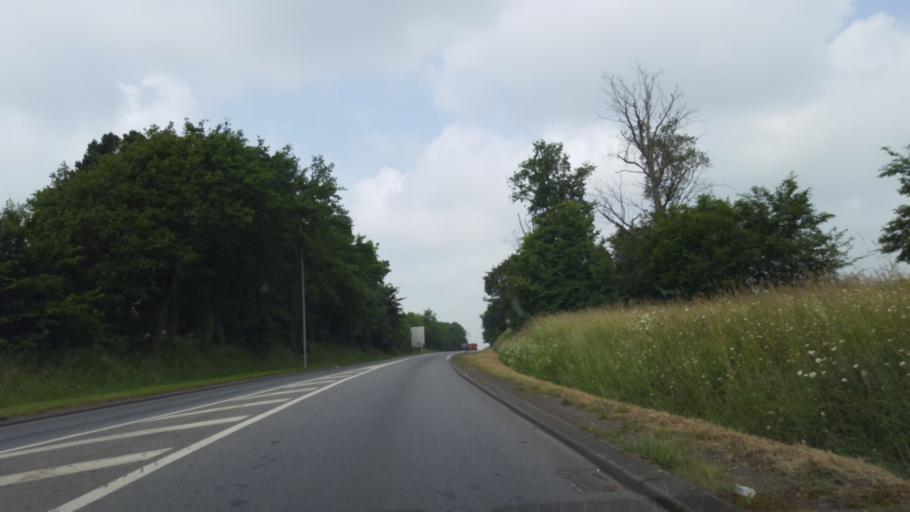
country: FR
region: Brittany
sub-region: Departement d'Ille-et-Vilaine
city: Chartres-de-Bretagne
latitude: 48.0433
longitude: -1.6968
